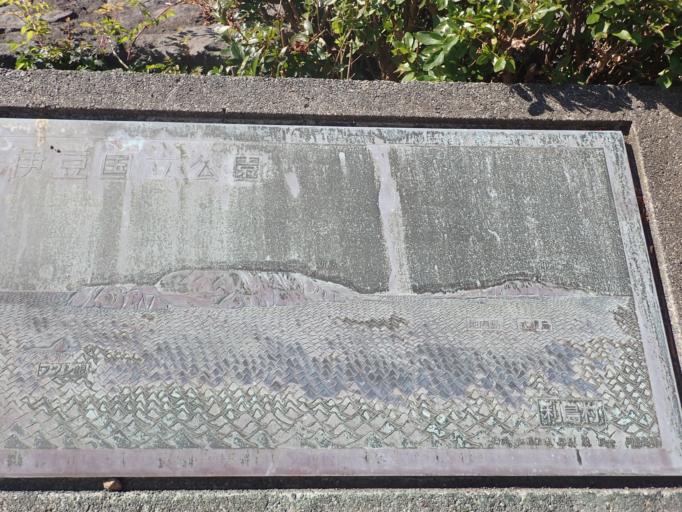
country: JP
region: Shizuoka
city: Shimoda
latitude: 34.5146
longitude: 139.2767
